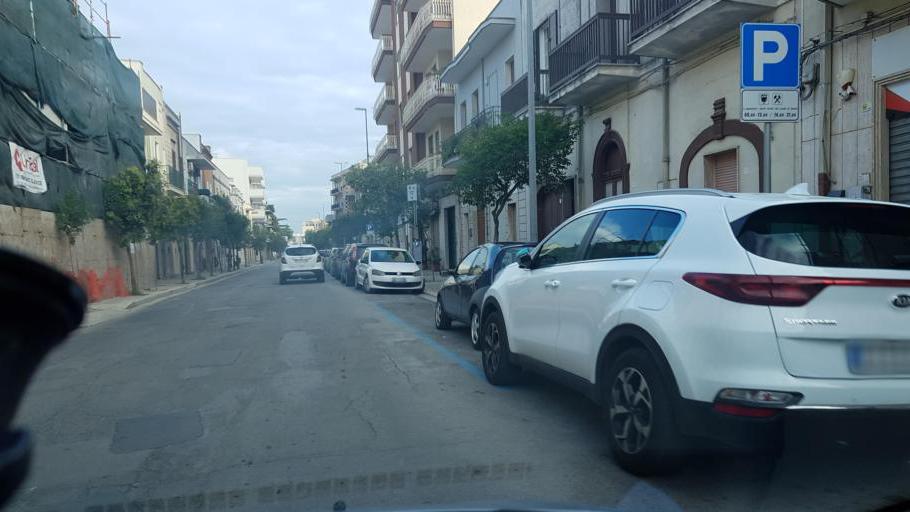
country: IT
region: Apulia
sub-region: Provincia di Brindisi
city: Francavilla Fontana
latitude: 40.5266
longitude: 17.5858
